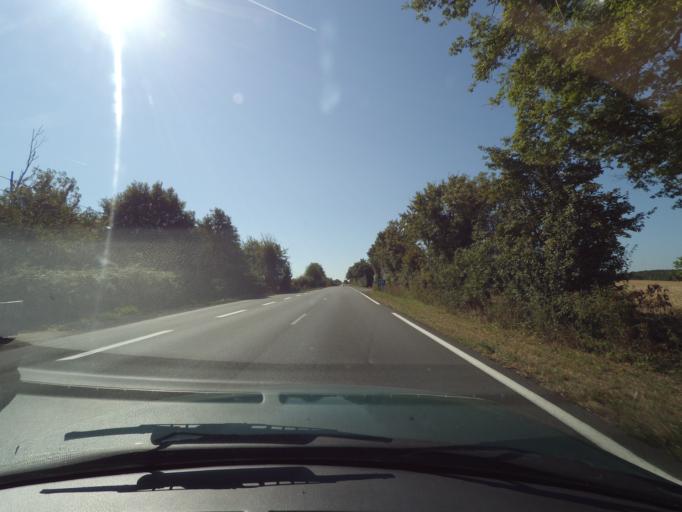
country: FR
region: Poitou-Charentes
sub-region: Departement de la Vienne
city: Saulge
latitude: 46.3115
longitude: 0.8287
